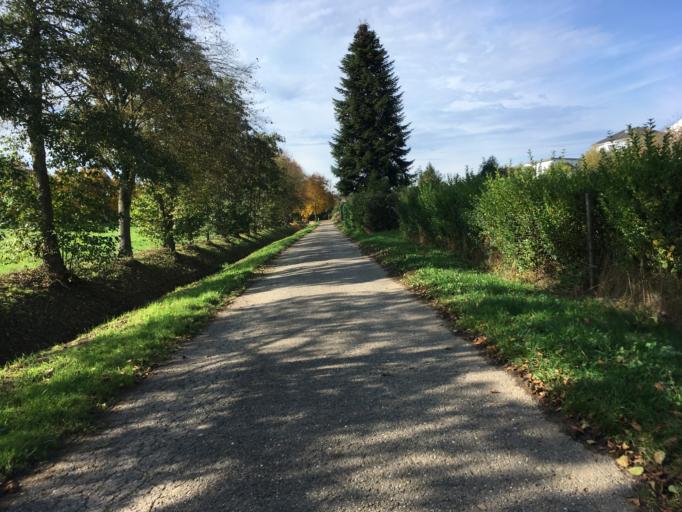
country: DE
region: Baden-Wuerttemberg
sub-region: Regierungsbezirk Stuttgart
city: Siegelsbach
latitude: 49.2536
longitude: 9.0492
